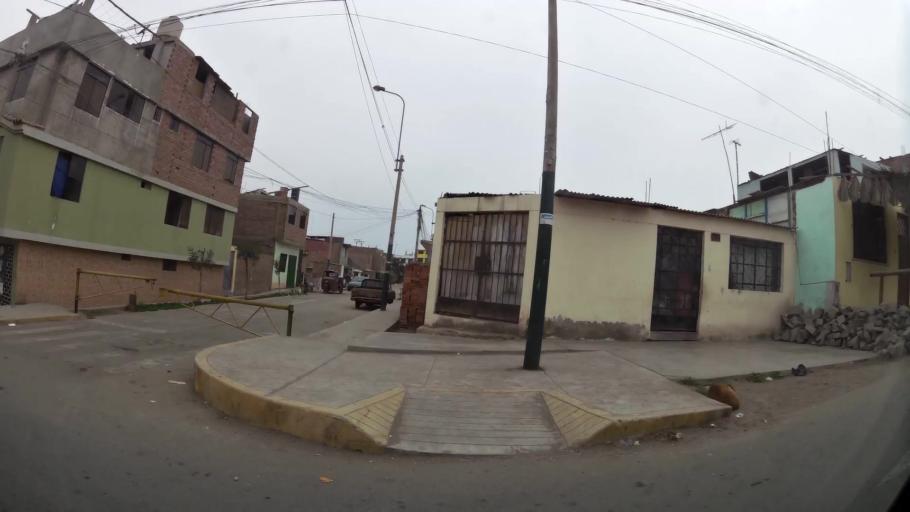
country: PE
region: Lima
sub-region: Lima
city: Surco
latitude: -12.1968
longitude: -76.9760
